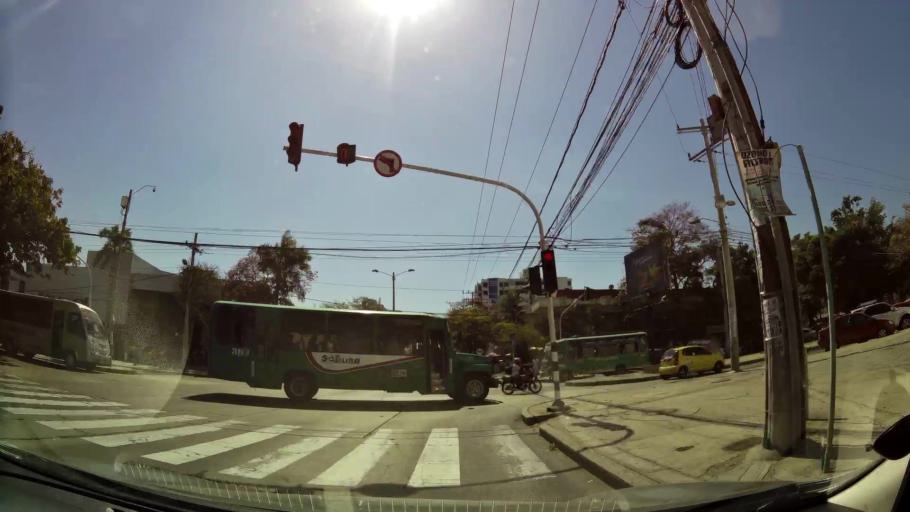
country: CO
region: Atlantico
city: Barranquilla
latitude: 10.9991
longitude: -74.8015
